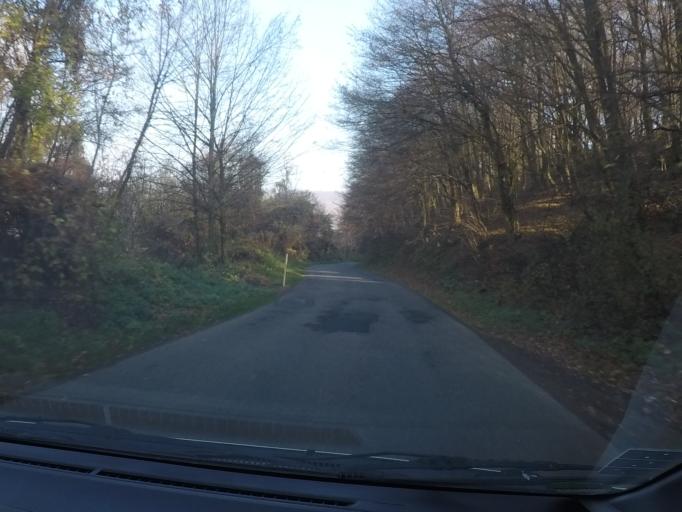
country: SK
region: Banskobystricky
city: Nova Bana
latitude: 48.4043
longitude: 18.6357
